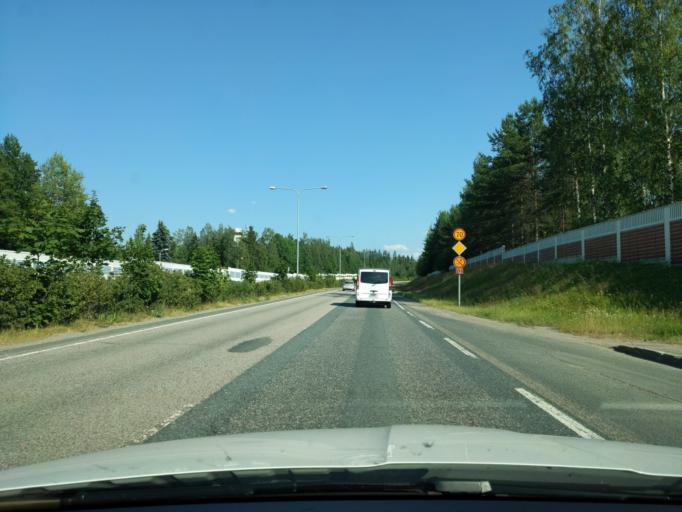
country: FI
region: Paijanne Tavastia
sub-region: Lahti
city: Lahti
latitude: 60.9849
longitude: 25.5806
